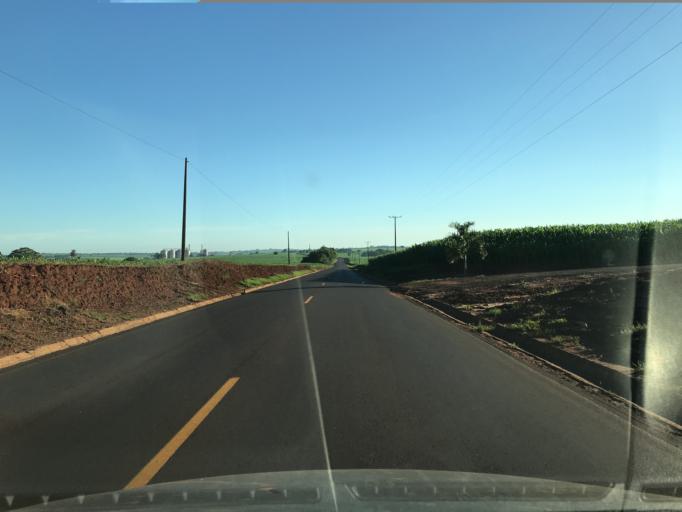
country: BR
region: Parana
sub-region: Palotina
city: Palotina
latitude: -24.1315
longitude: -53.8536
